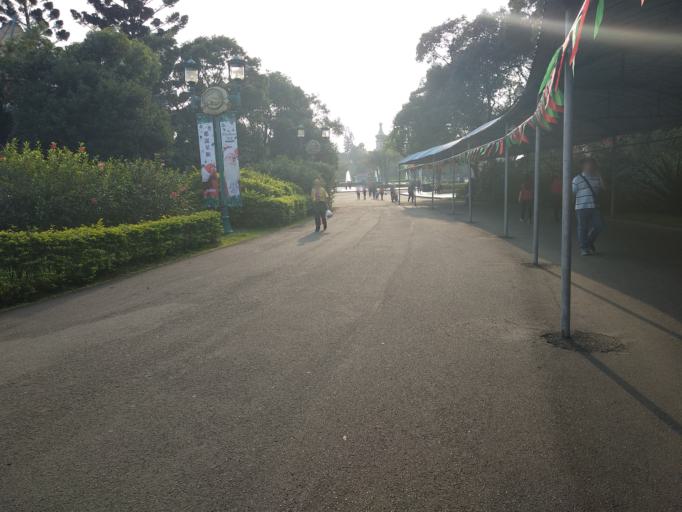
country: TW
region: Taiwan
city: Daxi
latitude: 24.8219
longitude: 121.1832
